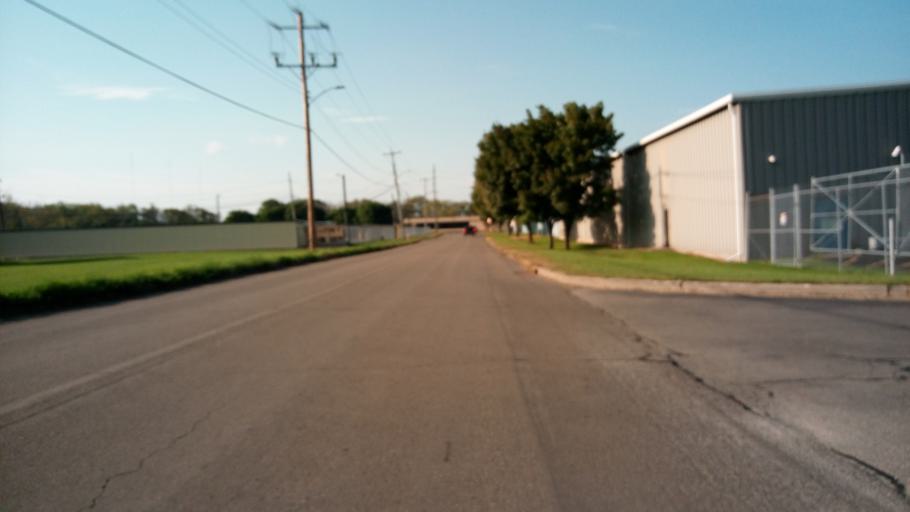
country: US
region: New York
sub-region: Chemung County
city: Elmira Heights
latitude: 42.1156
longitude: -76.8054
